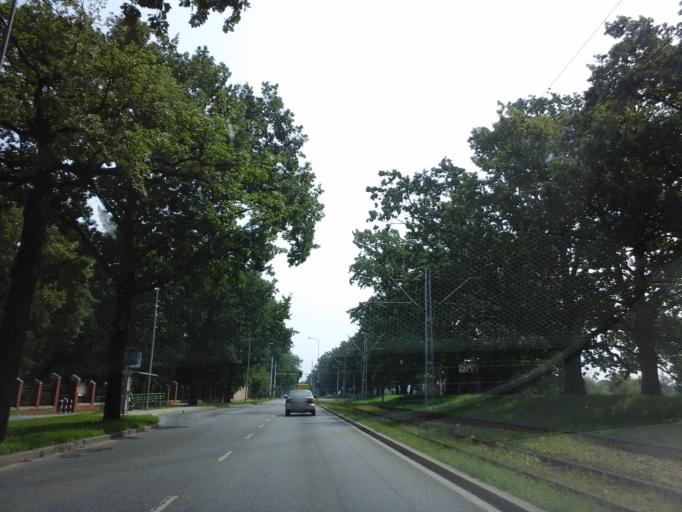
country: PL
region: Lower Silesian Voivodeship
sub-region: Powiat wroclawski
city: Wroclaw
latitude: 51.1349
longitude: 17.0085
